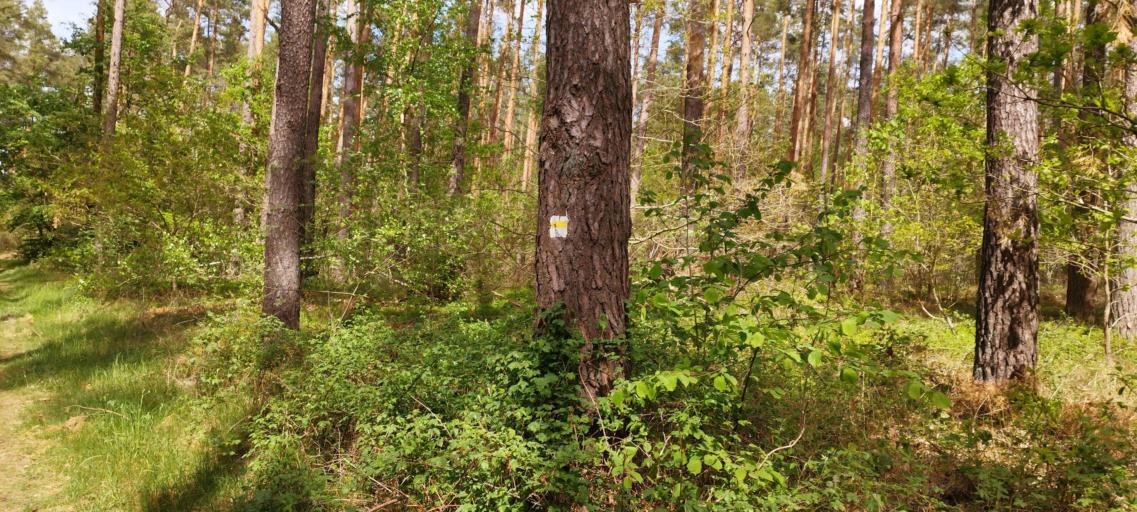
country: DE
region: Brandenburg
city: Grunheide
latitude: 52.4206
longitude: 13.8689
